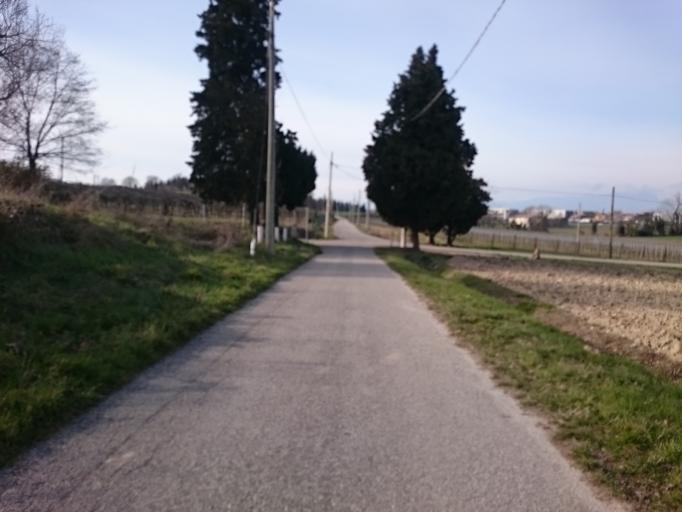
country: IT
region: Lombardy
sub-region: Provincia di Mantova
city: Ponti sul Mincio
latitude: 45.4248
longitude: 10.6904
